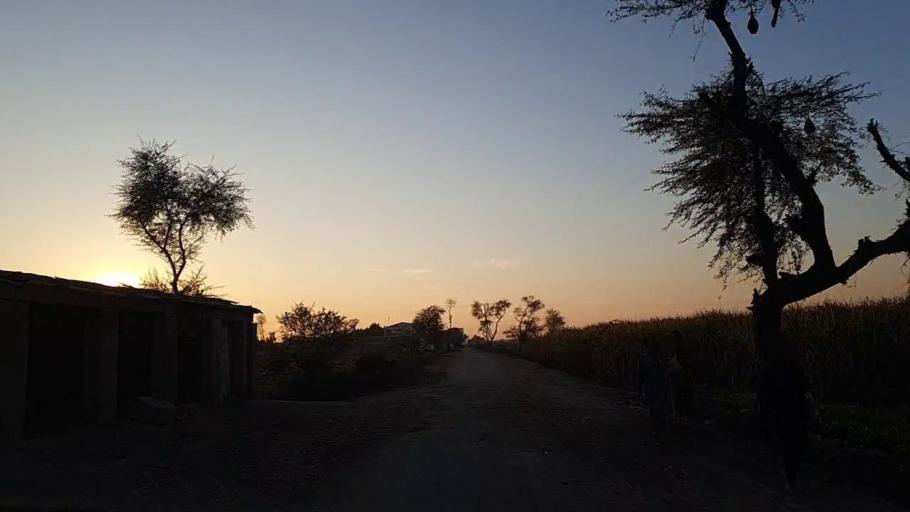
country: PK
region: Sindh
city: Bandhi
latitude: 26.6201
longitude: 68.3640
